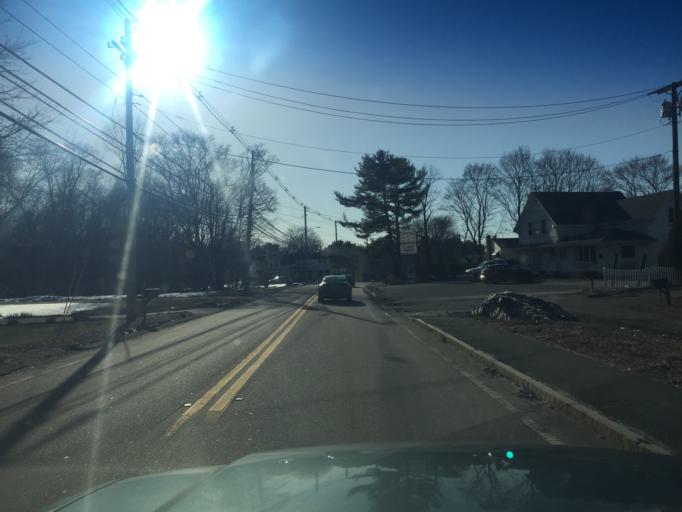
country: US
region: Massachusetts
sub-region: Norfolk County
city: Bellingham
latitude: 42.0867
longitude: -71.4812
